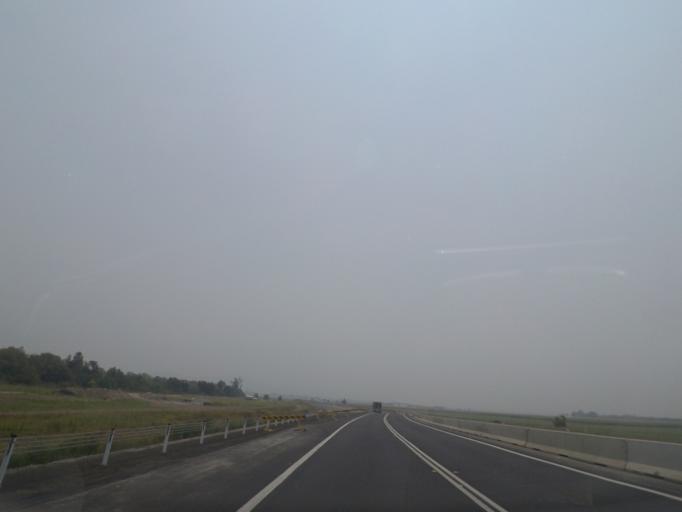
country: AU
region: New South Wales
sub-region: Clarence Valley
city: Maclean
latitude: -29.4038
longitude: 153.2423
